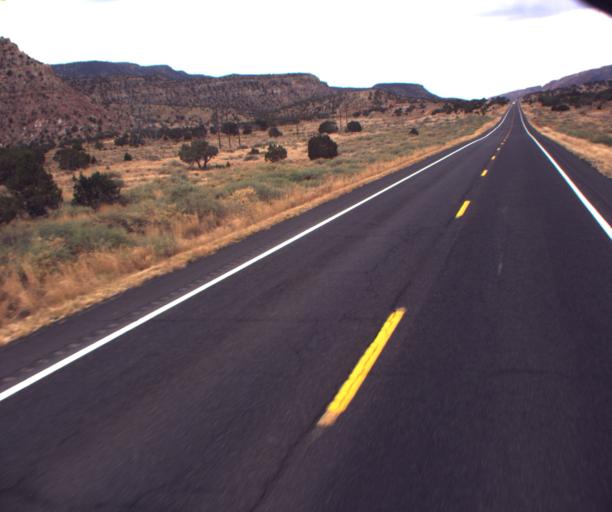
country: US
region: Arizona
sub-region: Navajo County
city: Kayenta
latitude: 36.6902
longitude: -110.3694
